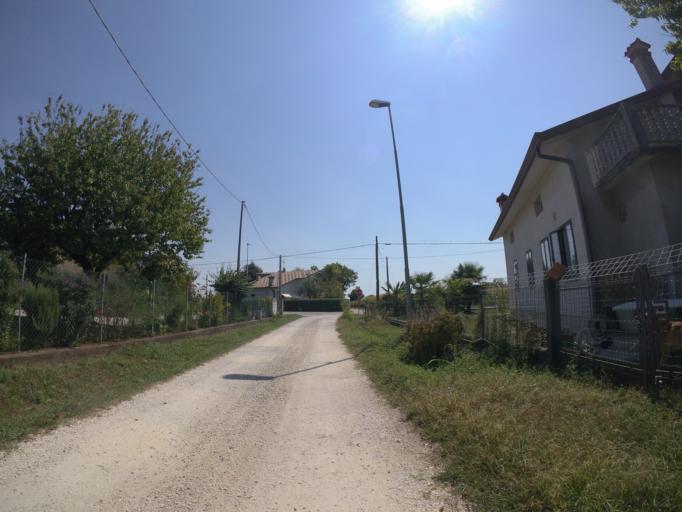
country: IT
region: Friuli Venezia Giulia
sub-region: Provincia di Udine
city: Bertiolo
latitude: 45.9434
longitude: 13.0299
